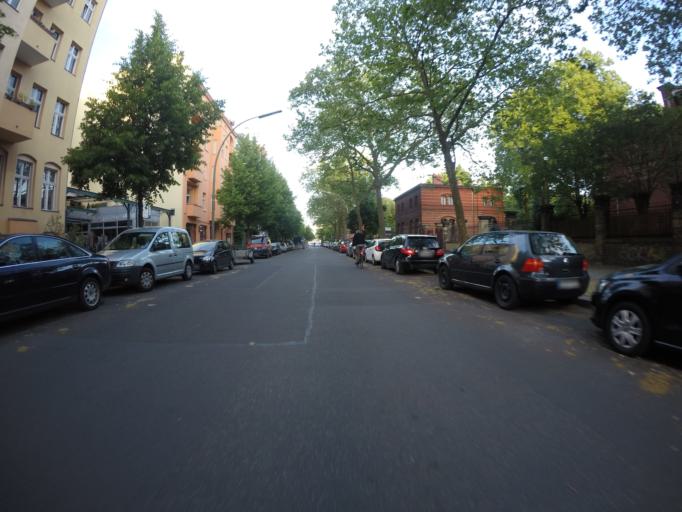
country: DE
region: Berlin
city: Bezirk Kreuzberg
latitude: 52.4888
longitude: 13.4035
